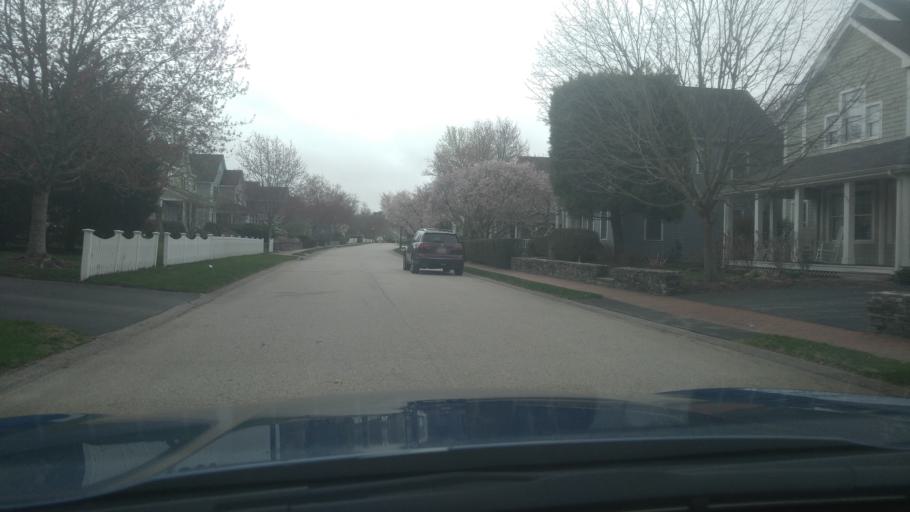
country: US
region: Rhode Island
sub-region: Washington County
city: North Kingstown
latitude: 41.5883
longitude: -71.4462
